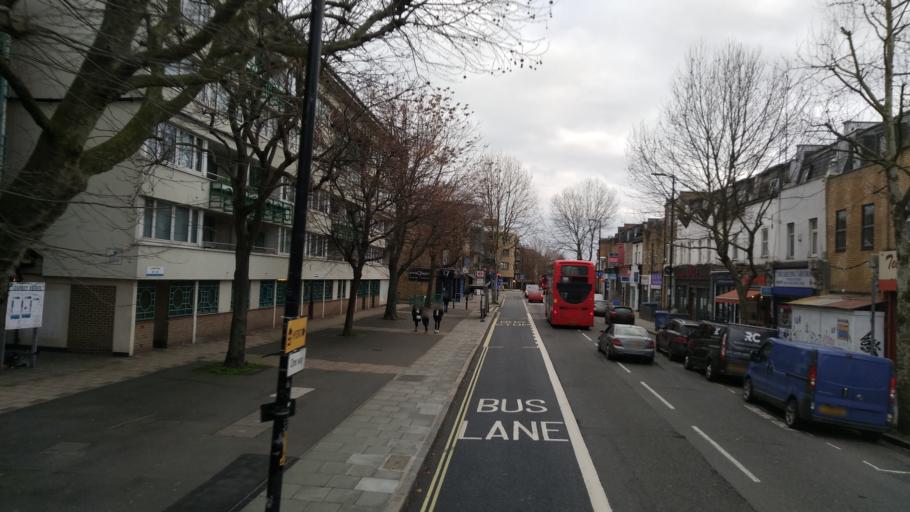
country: GB
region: England
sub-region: Greater London
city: Poplar
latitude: 51.4926
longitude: -0.0461
